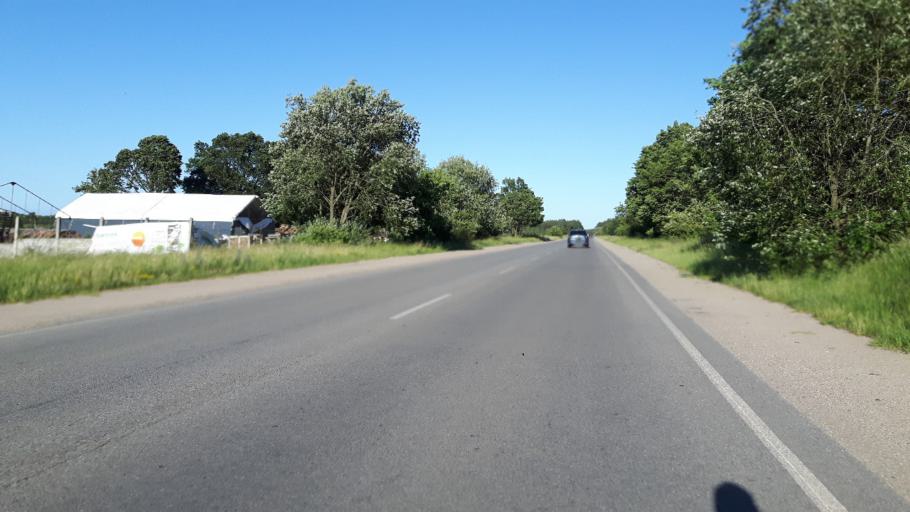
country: PL
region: Pomeranian Voivodeship
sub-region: Powiat pucki
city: Mrzezino
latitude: 54.6050
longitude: 18.4375
